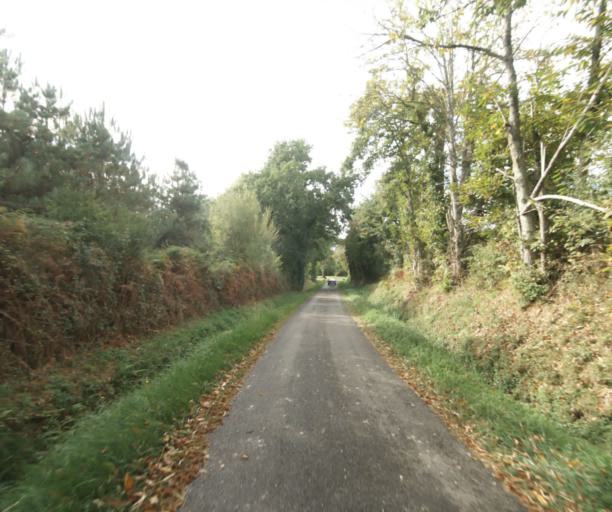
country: FR
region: Midi-Pyrenees
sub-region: Departement du Gers
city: Le Houga
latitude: 43.8605
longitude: -0.1325
